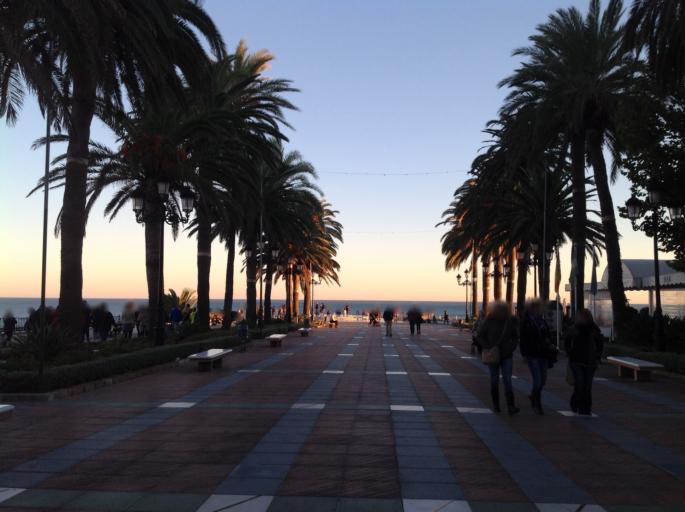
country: ES
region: Andalusia
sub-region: Provincia de Malaga
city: Nerja
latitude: 36.7450
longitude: -3.8759
